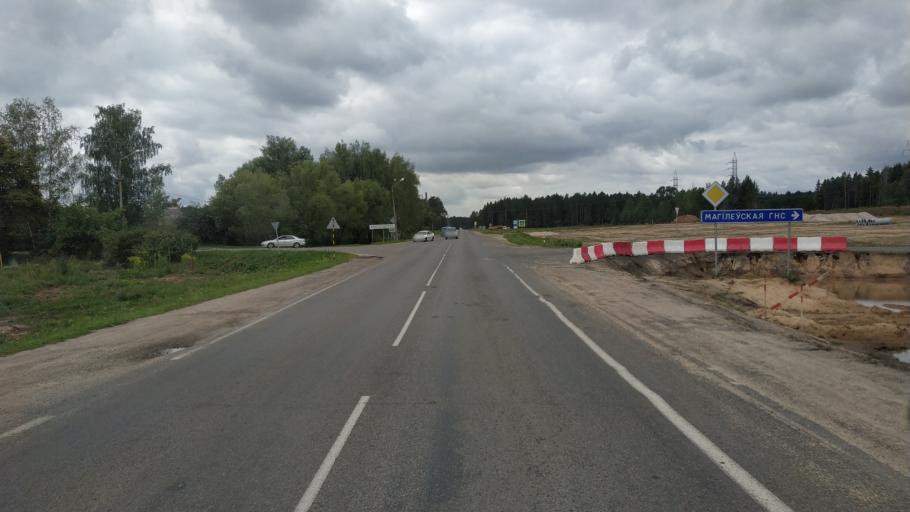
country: BY
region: Mogilev
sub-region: Mahilyowski Rayon
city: Veyno
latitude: 53.8751
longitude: 30.4324
